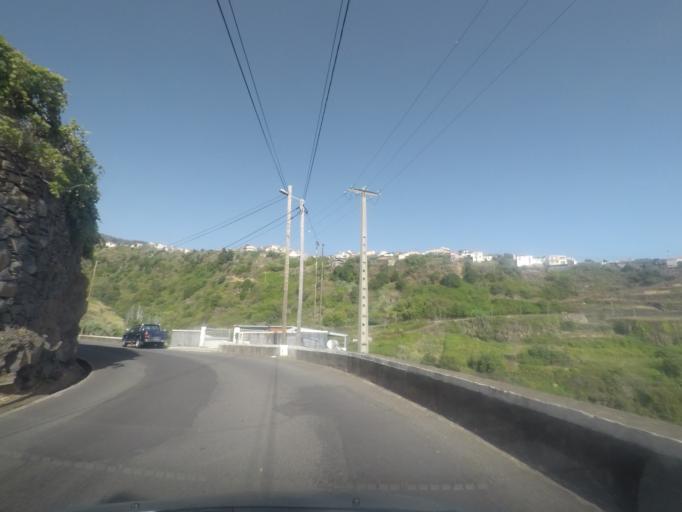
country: PT
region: Madeira
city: Calheta
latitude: 32.7294
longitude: -17.1677
